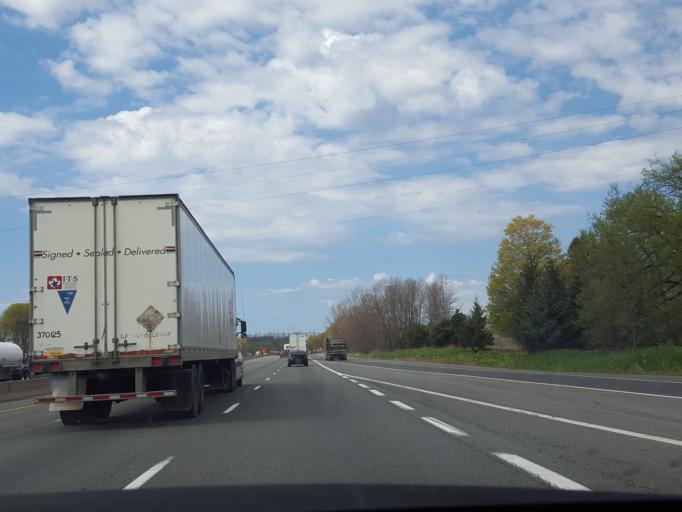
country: CA
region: Ontario
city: Oshawa
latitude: 43.8928
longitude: -78.6935
